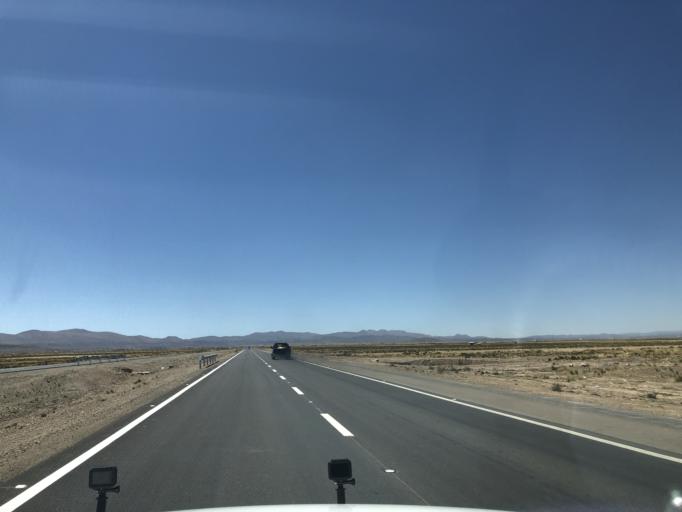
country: BO
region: La Paz
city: Colquiri
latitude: -17.6495
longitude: -67.1945
